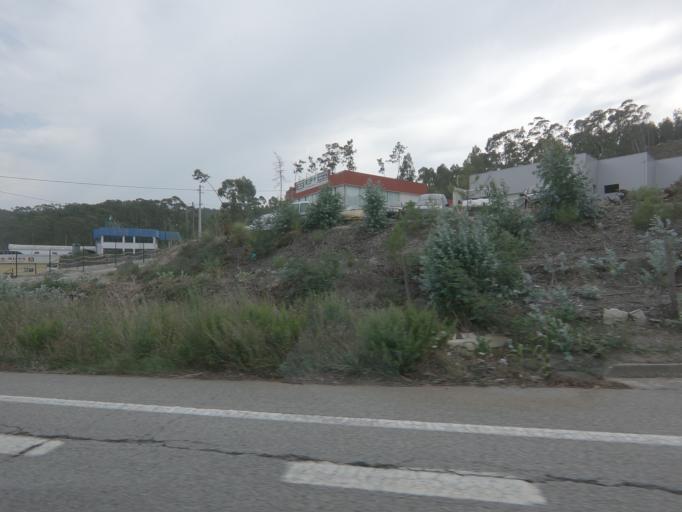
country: PT
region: Coimbra
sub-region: Penacova
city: Lorvao
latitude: 40.3040
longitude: -8.3216
